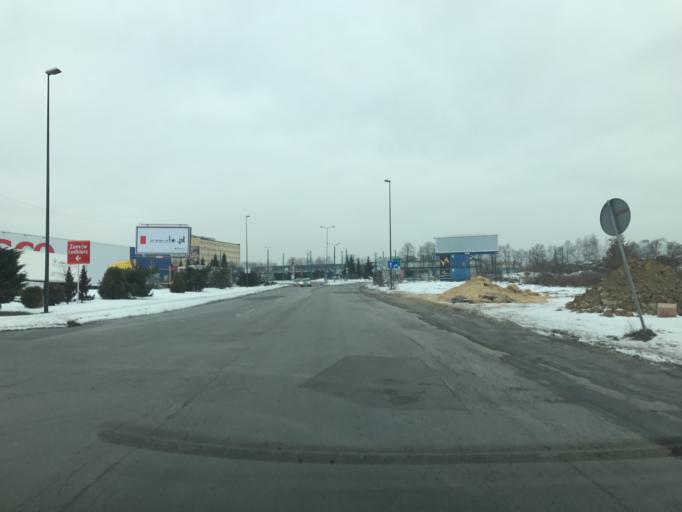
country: PL
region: Silesian Voivodeship
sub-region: Tychy
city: Cielmice
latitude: 50.0983
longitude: 19.0107
